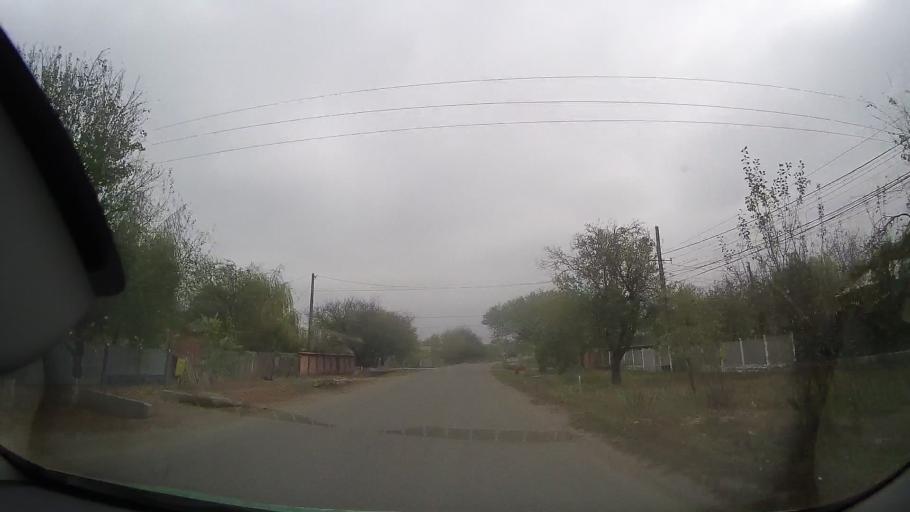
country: RO
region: Buzau
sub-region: Comuna Glodeanu-Silistea
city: Glodeanu-Silistea
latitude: 44.8209
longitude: 26.8337
